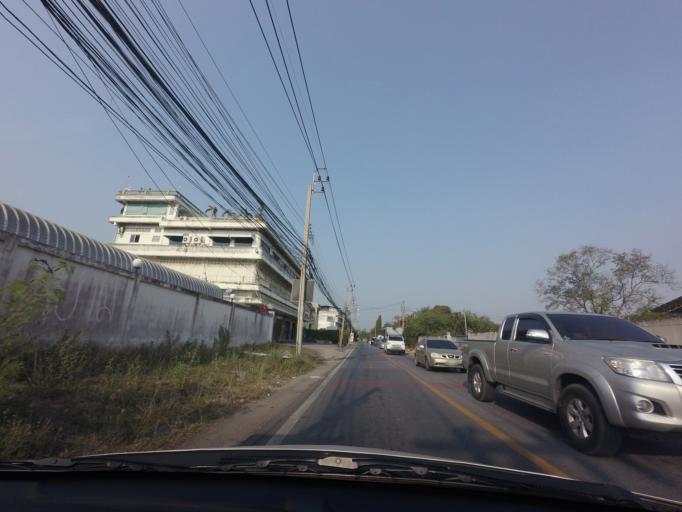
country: TH
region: Nonthaburi
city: Bang Yai
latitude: 13.8041
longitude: 100.4043
